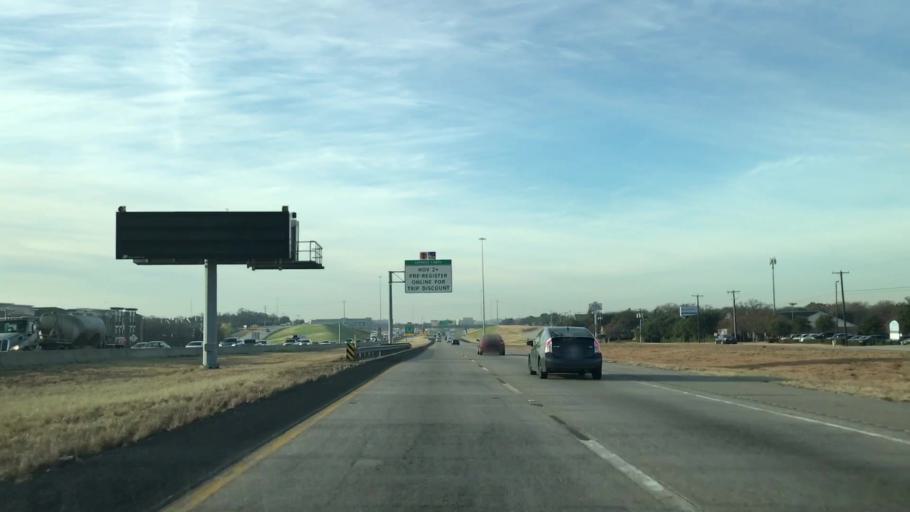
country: US
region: Texas
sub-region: Tarrant County
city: Bedford
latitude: 32.8499
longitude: -97.1123
